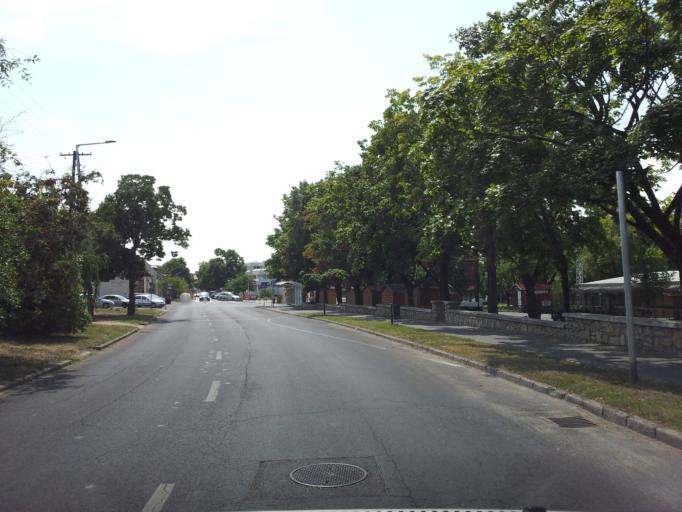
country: HU
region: Veszprem
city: Tapolca
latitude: 46.8852
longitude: 17.4434
